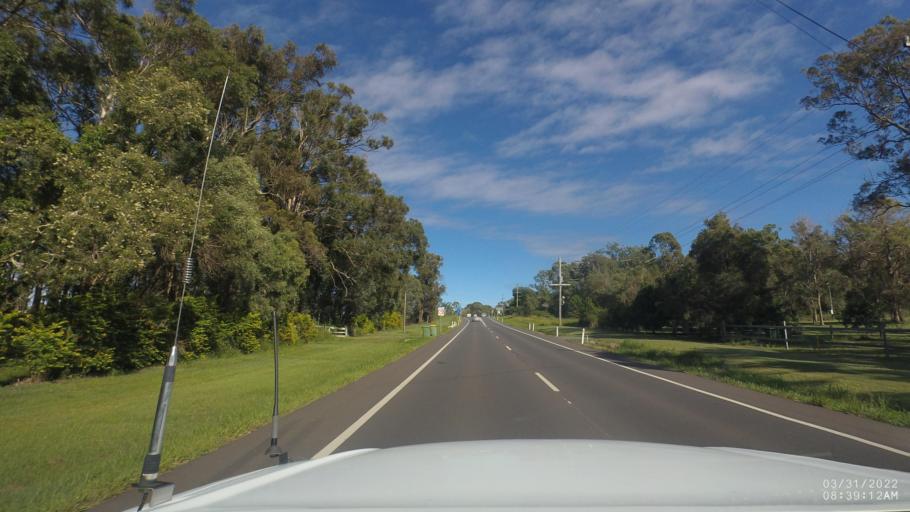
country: AU
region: Queensland
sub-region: Gold Coast
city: Yatala
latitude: -27.6768
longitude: 153.2313
